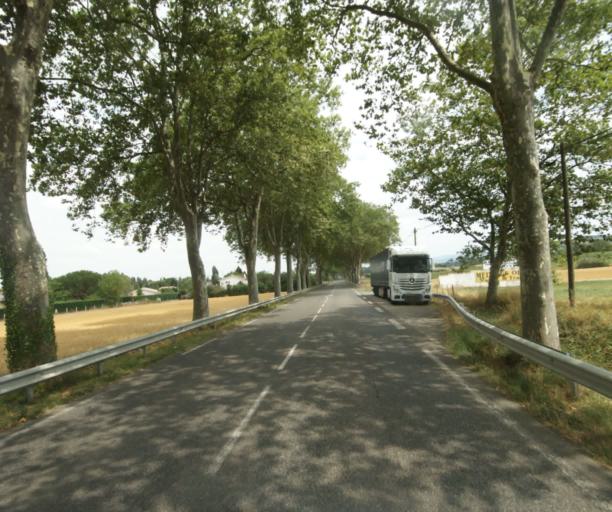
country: FR
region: Midi-Pyrenees
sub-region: Departement de la Haute-Garonne
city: Revel
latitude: 43.4489
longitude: 1.9681
